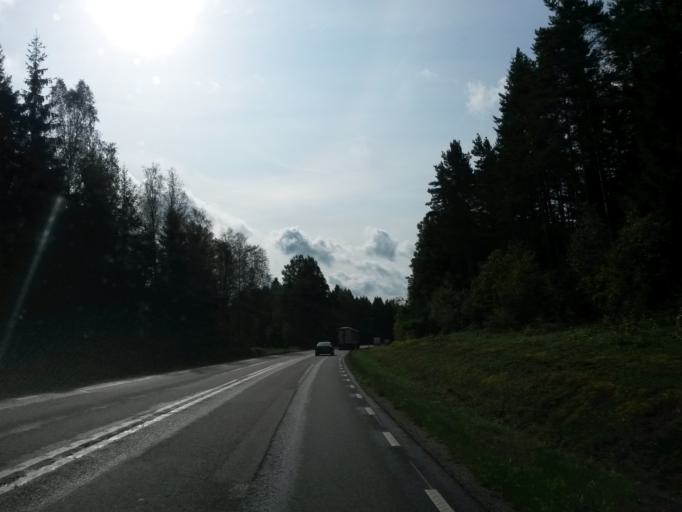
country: SE
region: Joenkoeping
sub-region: Varnamo Kommun
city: Rydaholm
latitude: 56.9240
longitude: 14.4170
